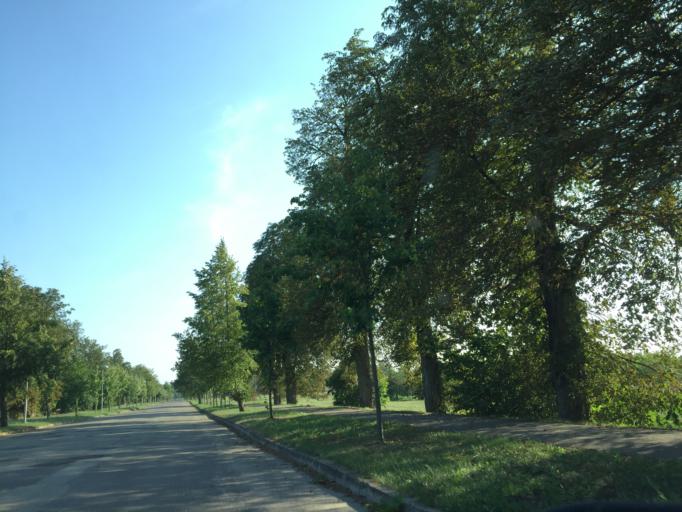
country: LT
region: Siauliu apskritis
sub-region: Joniskis
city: Joniskis
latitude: 56.4220
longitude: 23.7000
